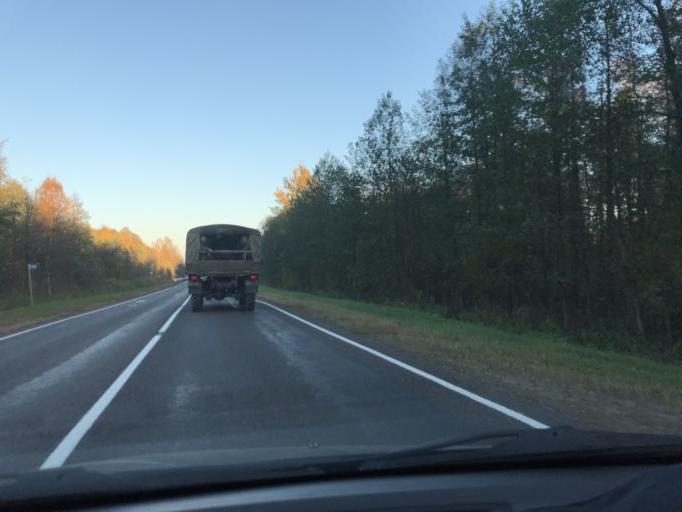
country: BY
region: Minsk
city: Staryya Darohi
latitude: 53.0430
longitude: 28.1433
